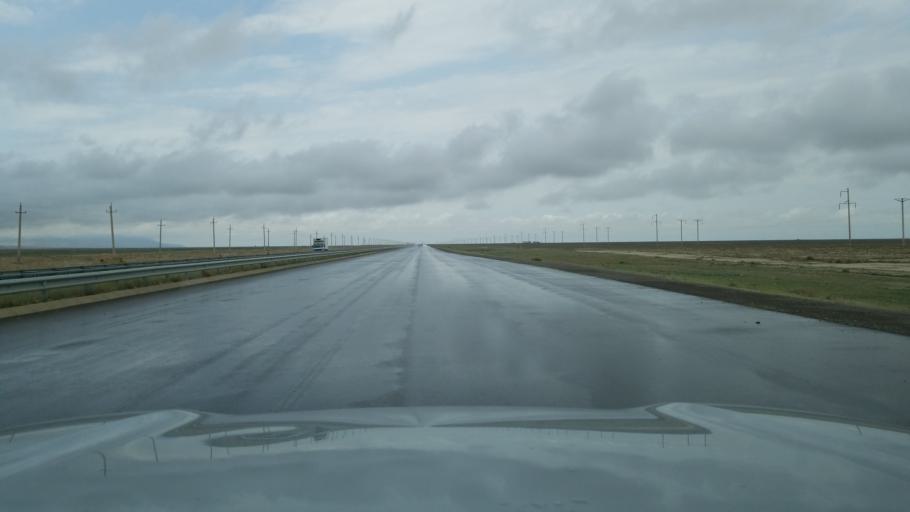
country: TM
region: Balkan
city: Gazanjyk
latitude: 39.1348
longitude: 55.8830
